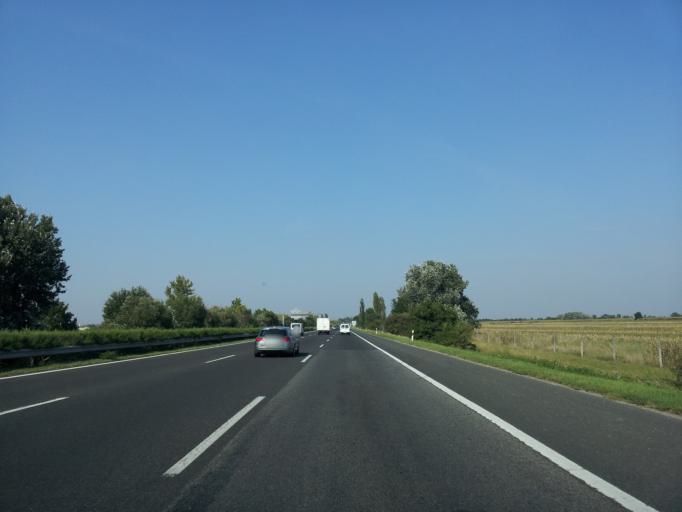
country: HU
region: Fejer
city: Szekesfehervar
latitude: 47.1578
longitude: 18.4482
